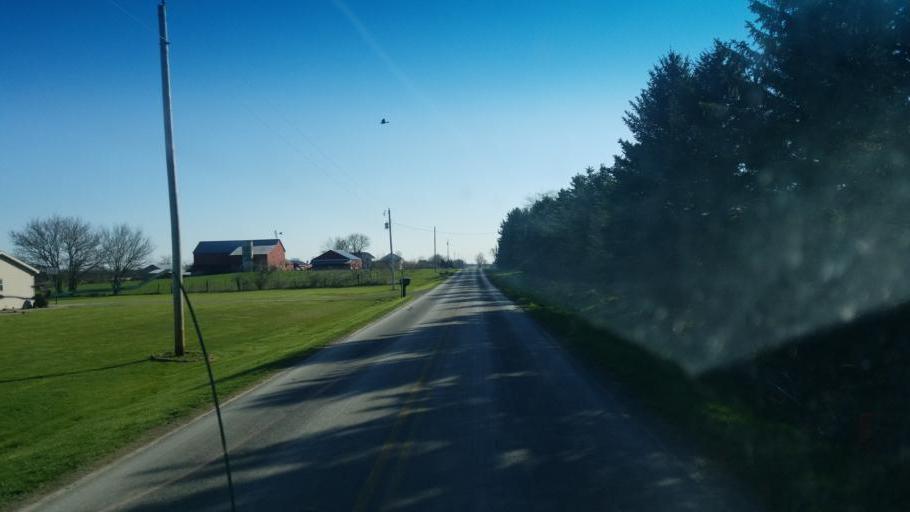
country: US
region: Ohio
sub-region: Hardin County
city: Kenton
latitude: 40.5454
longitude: -83.6001
